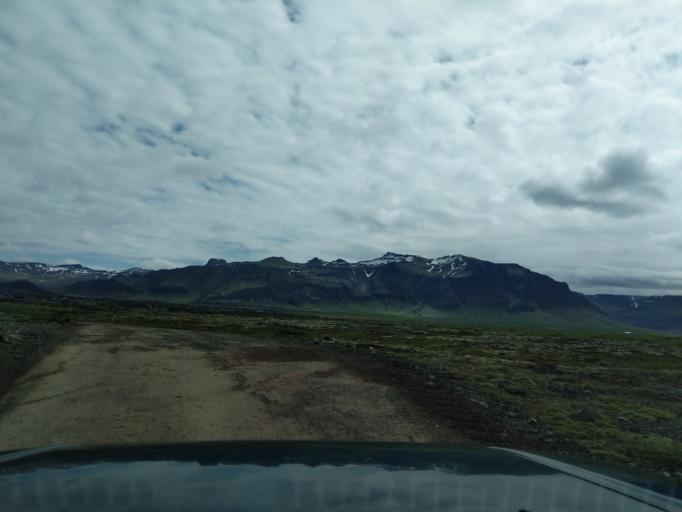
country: IS
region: West
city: Stykkisholmur
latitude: 64.8338
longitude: -22.3105
